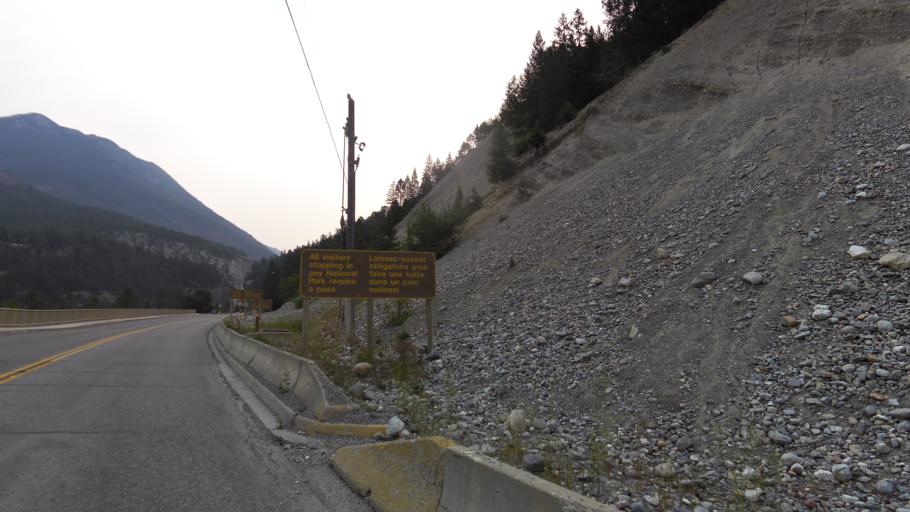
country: CA
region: British Columbia
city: Invermere
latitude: 50.6300
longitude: -116.0638
